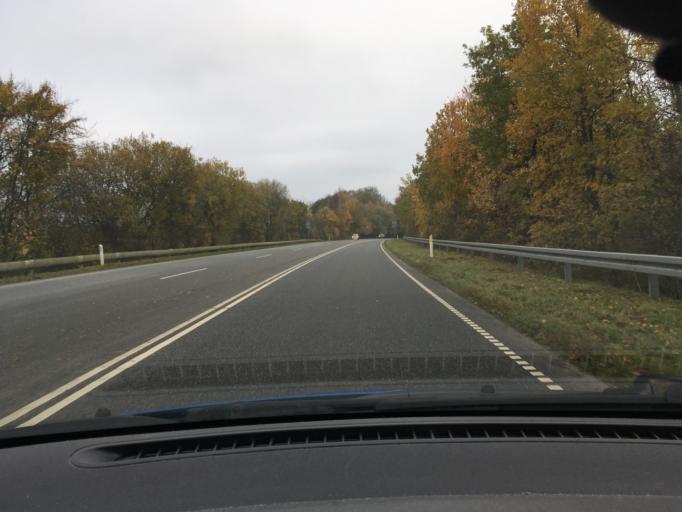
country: DK
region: South Denmark
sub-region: Aabenraa Kommune
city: Aabenraa
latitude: 55.0097
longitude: 9.4206
